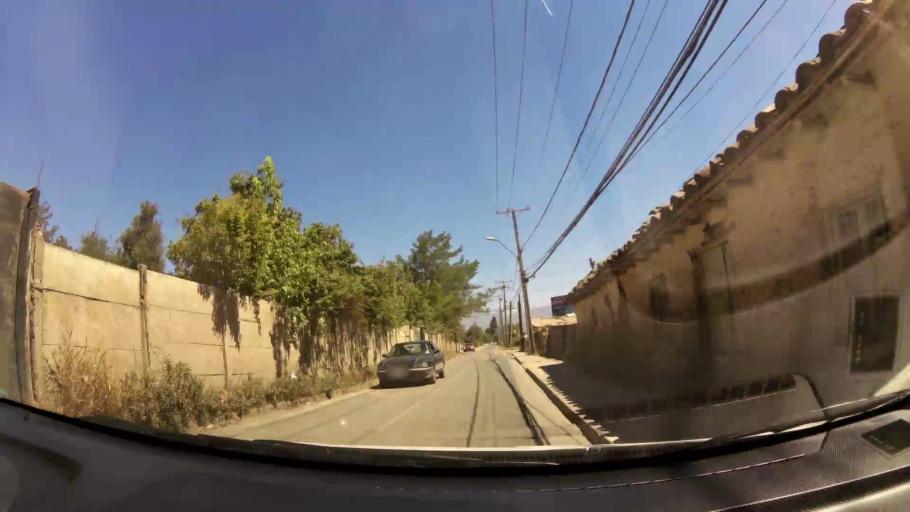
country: CL
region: O'Higgins
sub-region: Provincia de Cachapoal
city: Rancagua
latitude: -34.1471
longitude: -70.7235
